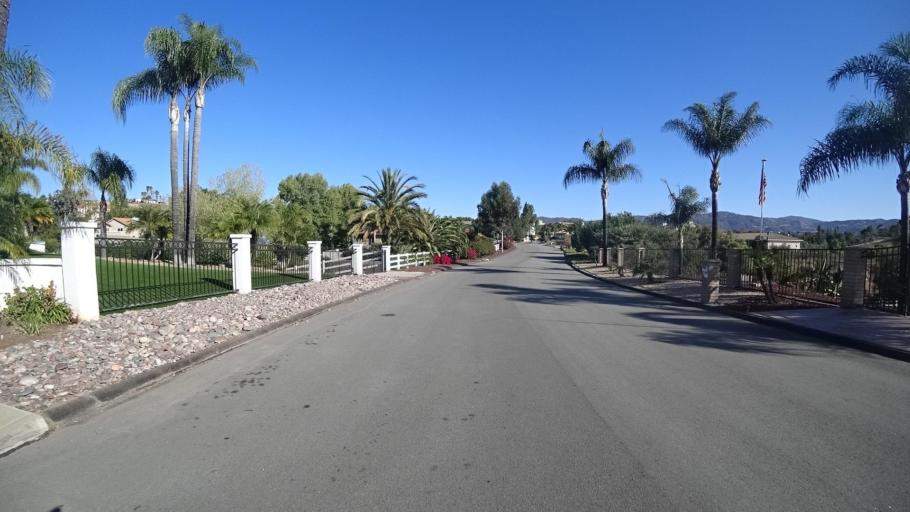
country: US
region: California
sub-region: San Diego County
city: Jamul
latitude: 32.7083
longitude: -116.8744
